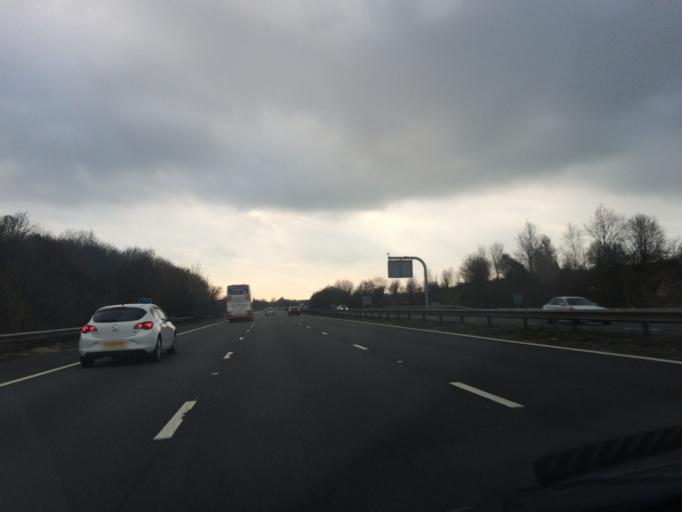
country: GB
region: England
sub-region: West Berkshire
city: Hungerford
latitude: 51.4537
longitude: -1.4853
